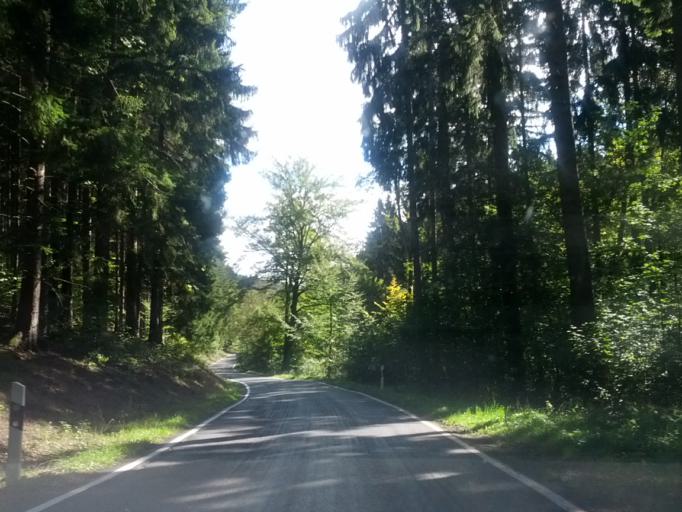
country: DE
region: Thuringia
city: Ruhla
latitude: 50.8935
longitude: 10.3450
